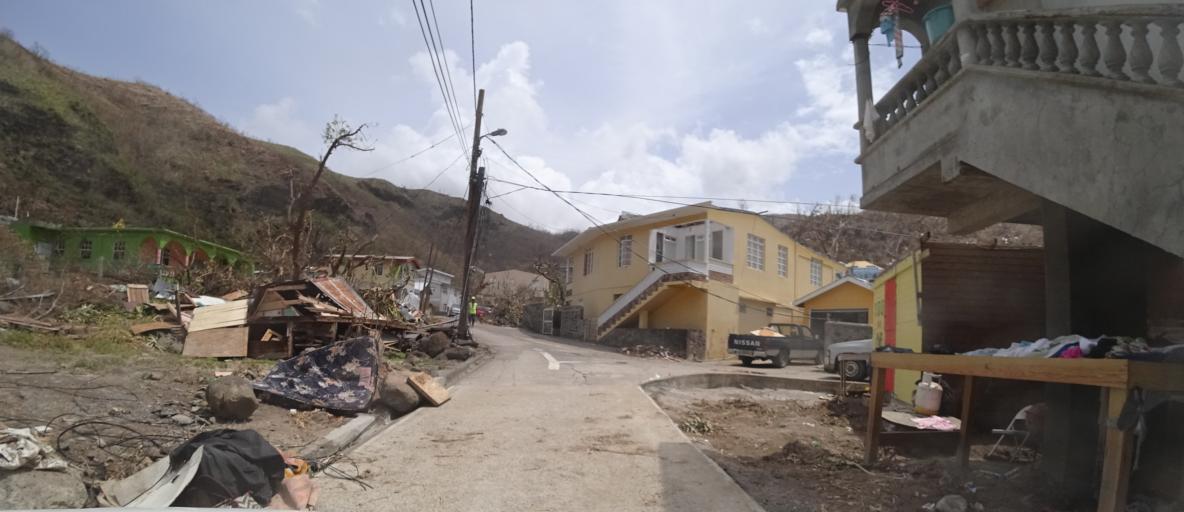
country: DM
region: Saint Peter
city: Colihaut
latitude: 15.4865
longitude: -61.4615
